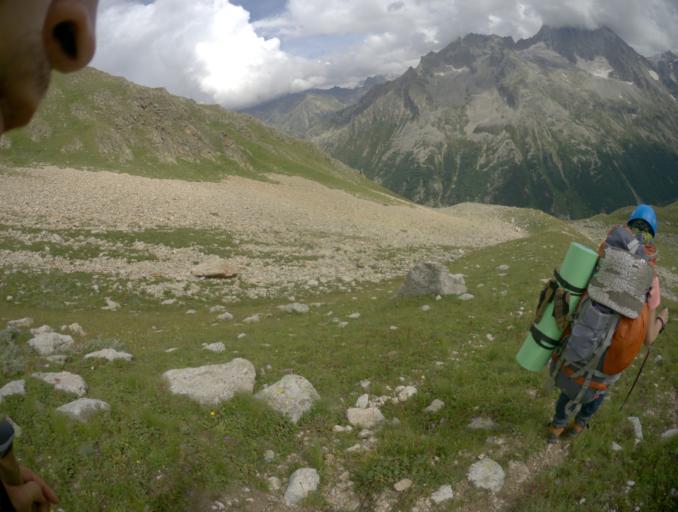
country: RU
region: Karachayevo-Cherkesiya
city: Uchkulan
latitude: 43.2710
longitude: 42.1255
